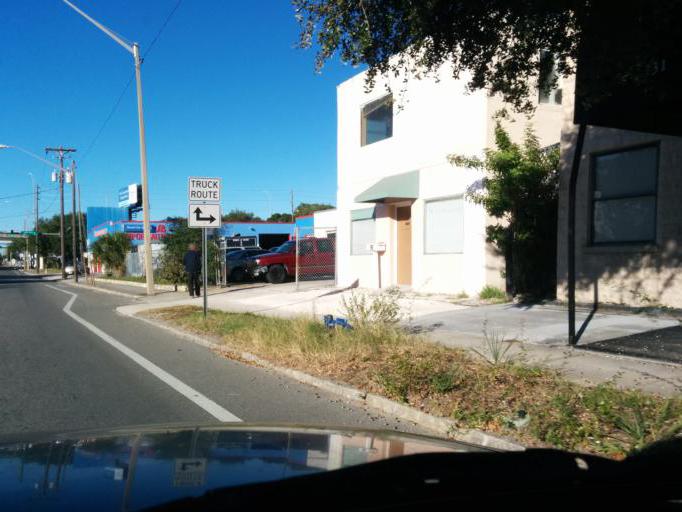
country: US
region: Florida
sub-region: Pinellas County
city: Saint Petersburg
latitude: 27.7755
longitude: -82.6548
